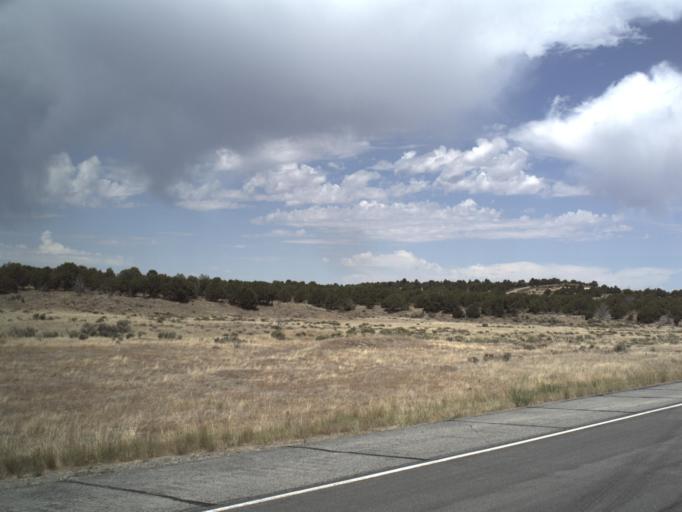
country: US
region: Utah
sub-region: Utah County
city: Eagle Mountain
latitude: 39.9821
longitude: -112.2616
